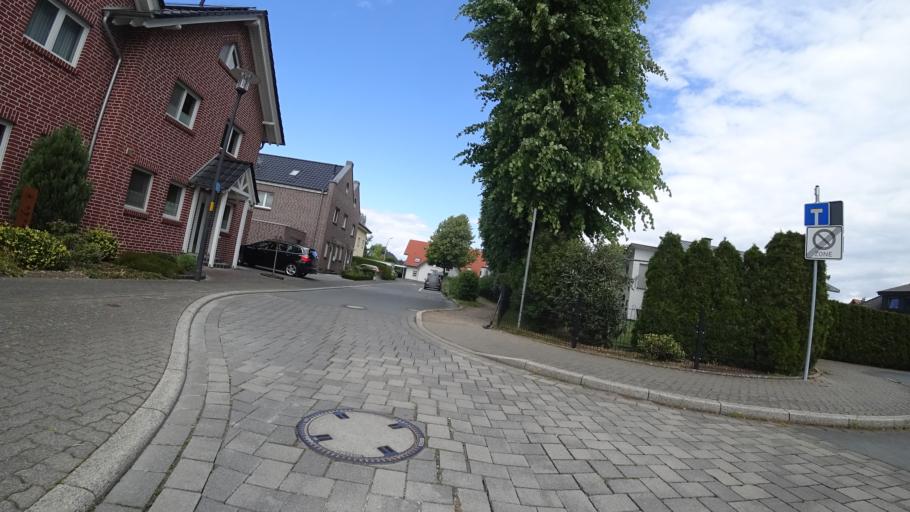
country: DE
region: North Rhine-Westphalia
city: Erwitte
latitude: 51.6316
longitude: 8.3704
